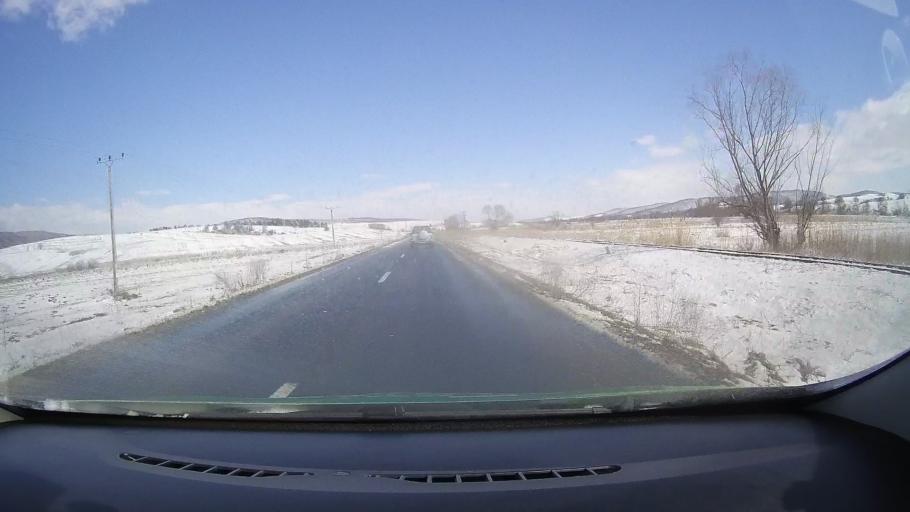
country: RO
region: Sibiu
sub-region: Comuna Rosia
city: Rosia
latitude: 45.8065
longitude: 24.3561
